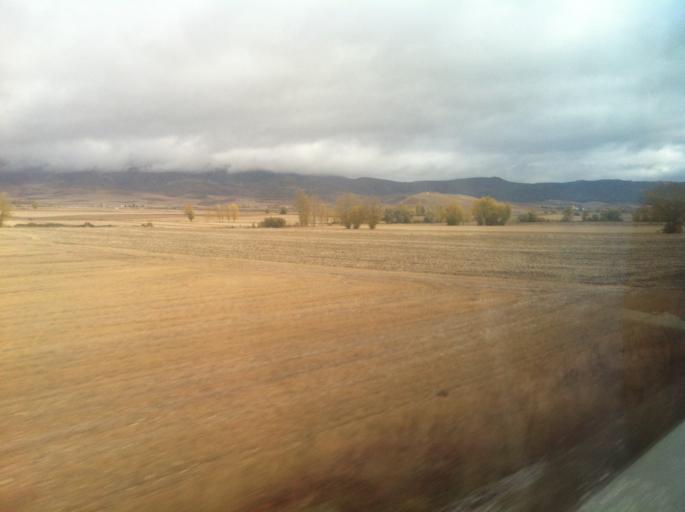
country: ES
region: Castille and Leon
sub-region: Provincia de Burgos
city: Cubo de Bureba
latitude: 42.6239
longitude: -3.2088
